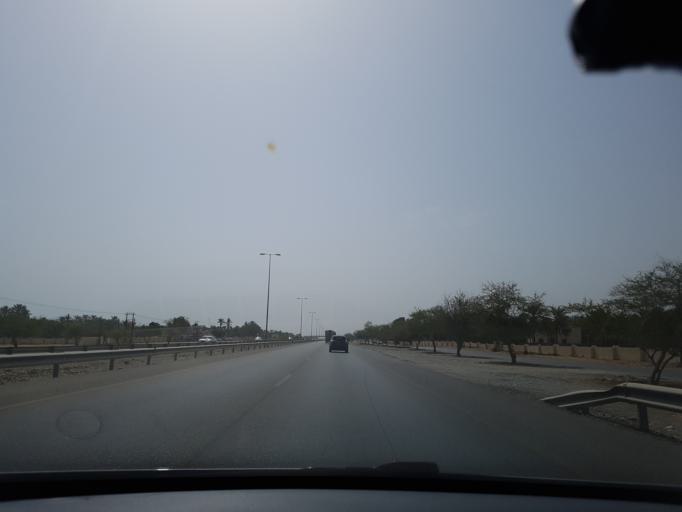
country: OM
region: Al Batinah
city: Al Khaburah
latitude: 23.9351
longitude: 57.1364
